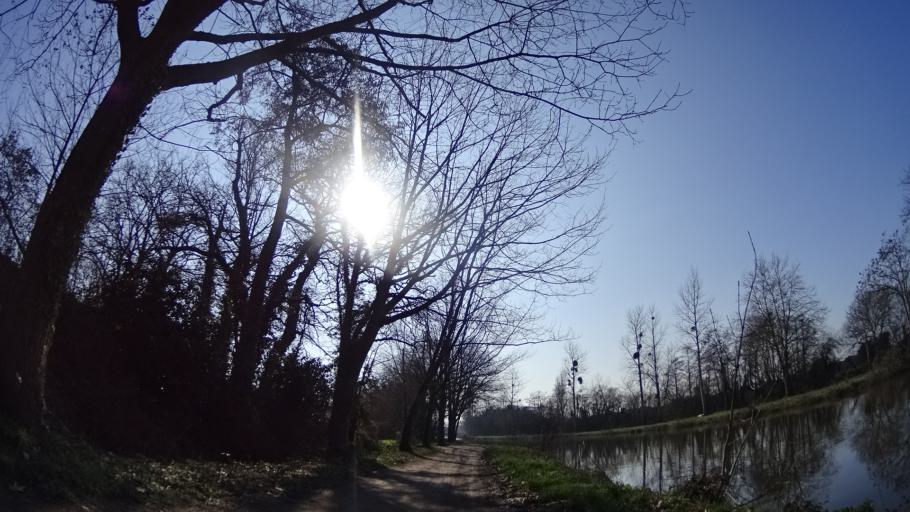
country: FR
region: Brittany
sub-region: Departement d'Ille-et-Vilaine
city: Saint-Gregoire
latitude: 48.1382
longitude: -1.6745
